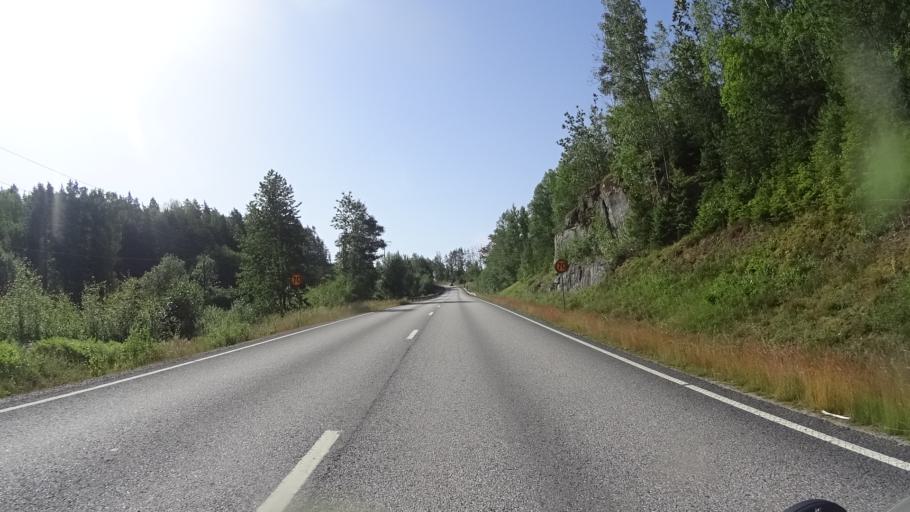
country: SE
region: Kalmar
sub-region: Vasterviks Kommun
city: Overum
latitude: 58.0489
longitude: 16.2091
